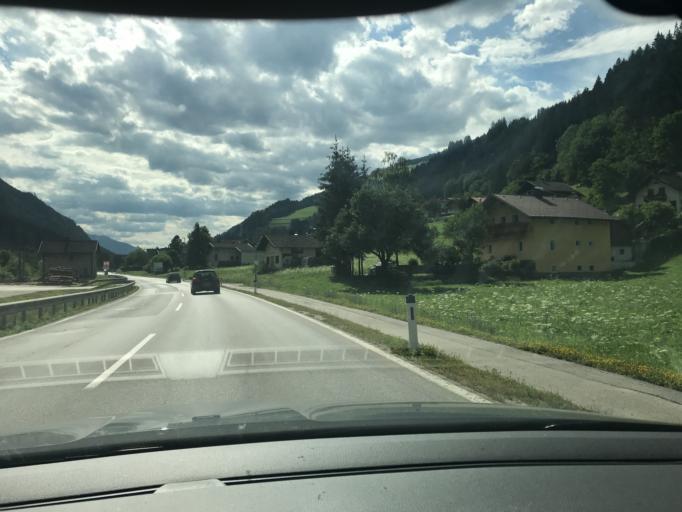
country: AT
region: Tyrol
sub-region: Politischer Bezirk Lienz
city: Leisach
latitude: 46.7845
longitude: 12.6707
